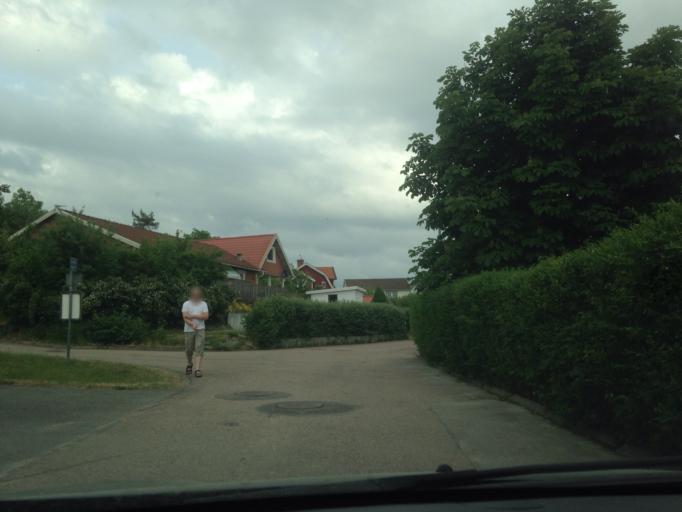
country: SE
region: Vaestra Goetaland
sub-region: Kungalvs Kommun
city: Kungalv
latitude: 57.8057
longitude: 11.9046
